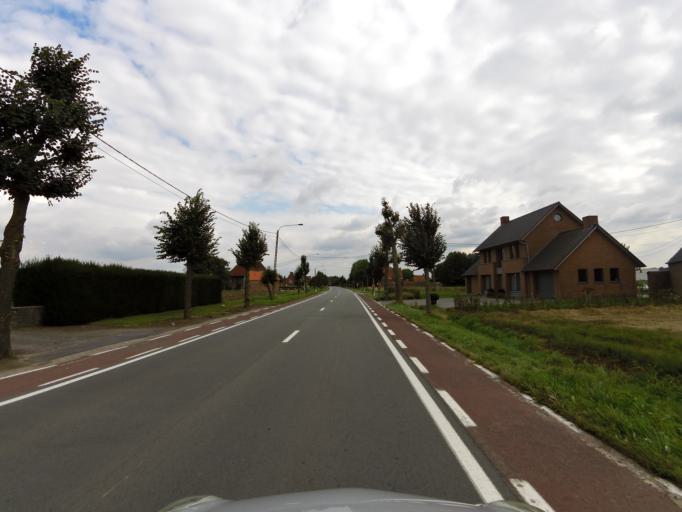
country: BE
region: Flanders
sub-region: Provincie West-Vlaanderen
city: Pittem
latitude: 50.9960
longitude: 3.2448
